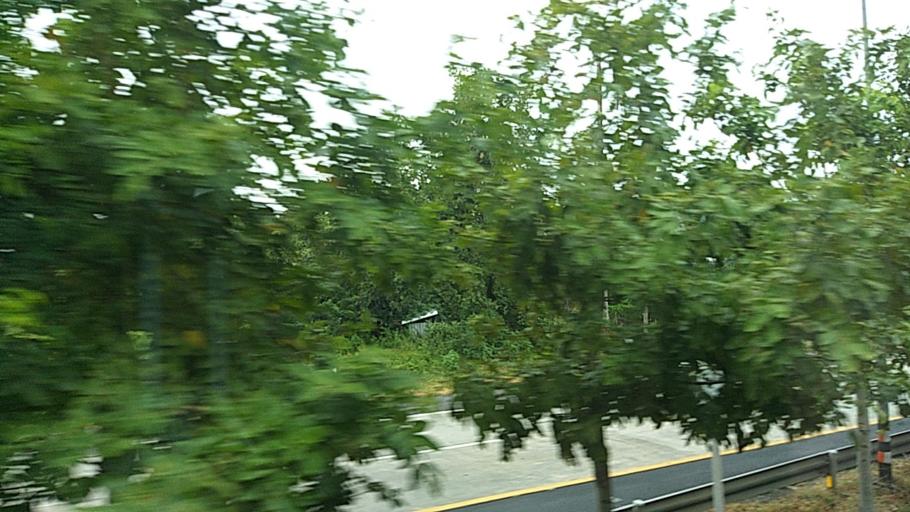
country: TH
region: Nakhon Ratchasima
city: Phimai
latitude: 15.2810
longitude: 102.4184
